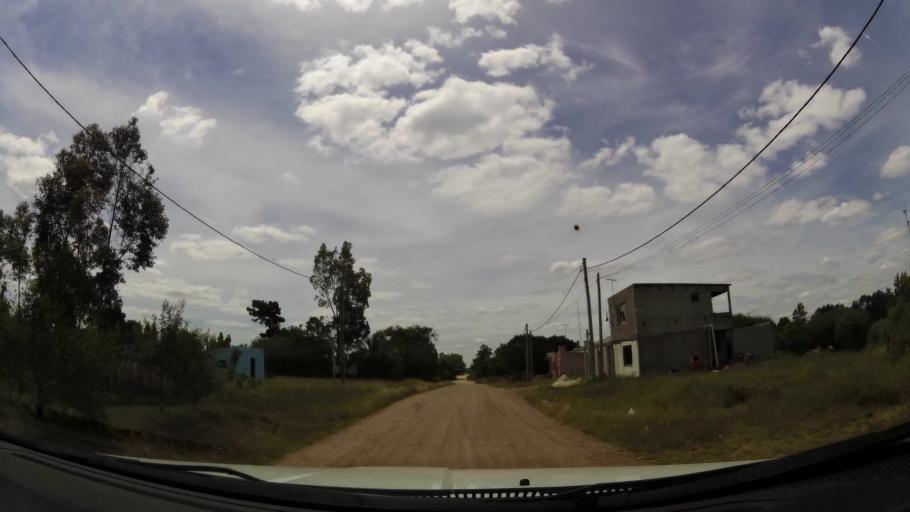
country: UY
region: San Jose
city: Delta del Tigre
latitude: -34.7542
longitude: -56.4163
